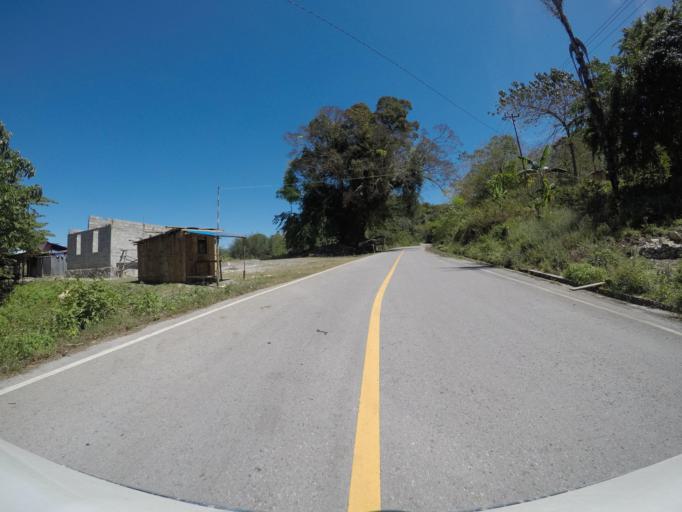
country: TL
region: Manatuto
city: Manatuto
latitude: -8.8064
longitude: 125.9709
